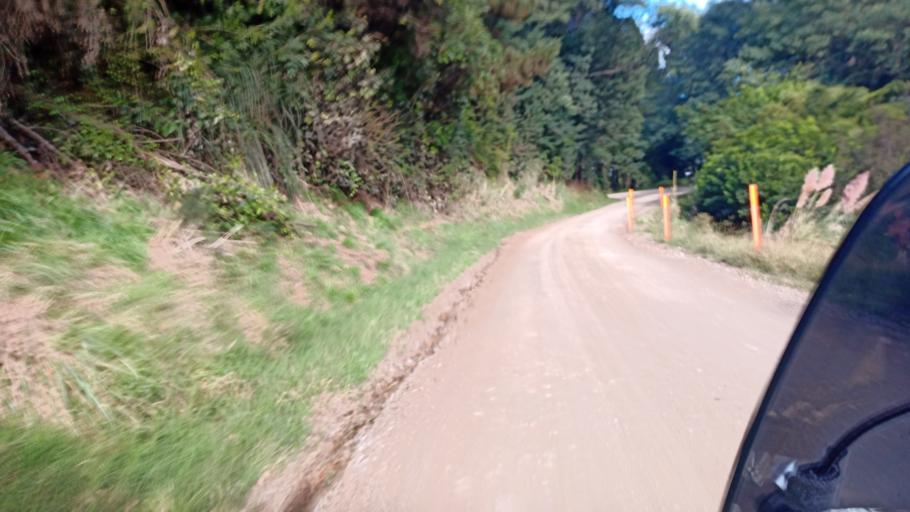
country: NZ
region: Gisborne
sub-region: Gisborne District
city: Gisborne
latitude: -38.5354
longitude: 177.5258
